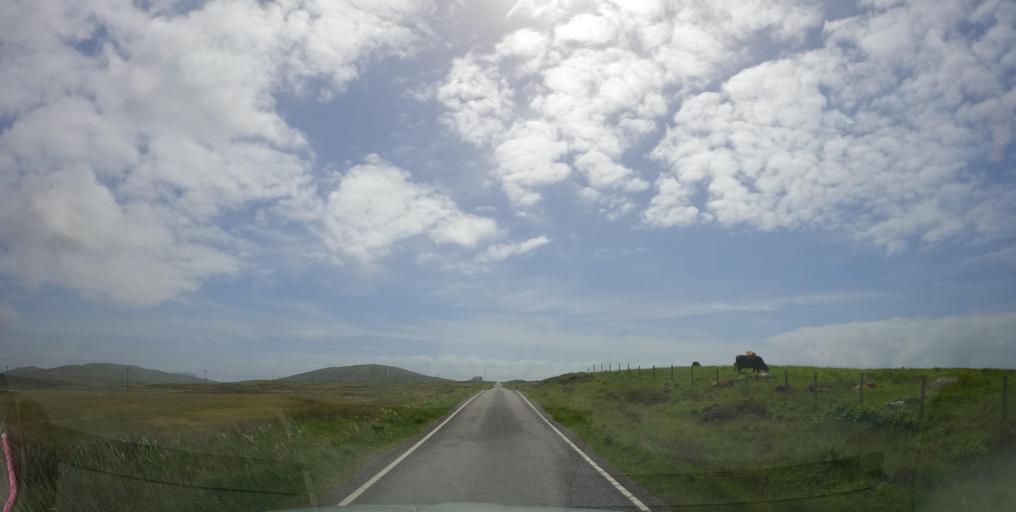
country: GB
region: Scotland
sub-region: Eilean Siar
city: Isle of South Uist
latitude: 57.2071
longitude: -7.3935
